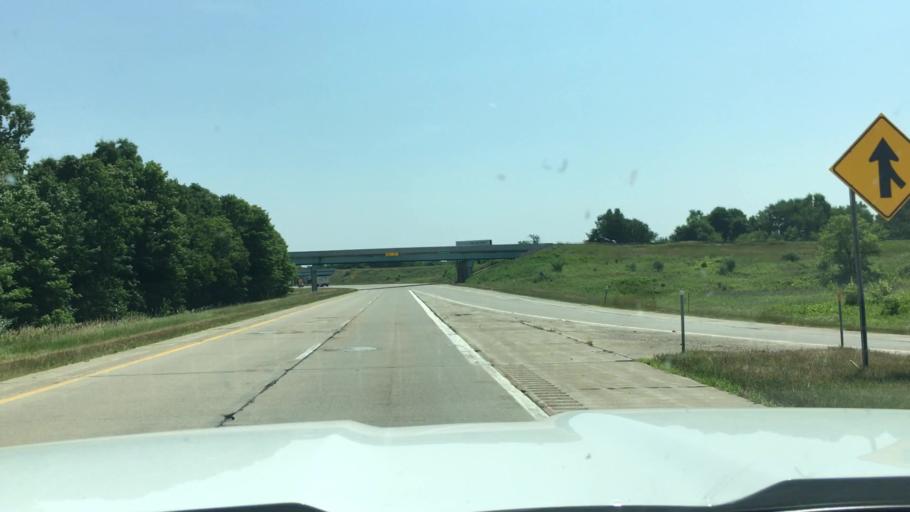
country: US
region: Michigan
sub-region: Clinton County
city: Wacousta
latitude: 42.7879
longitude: -84.6667
